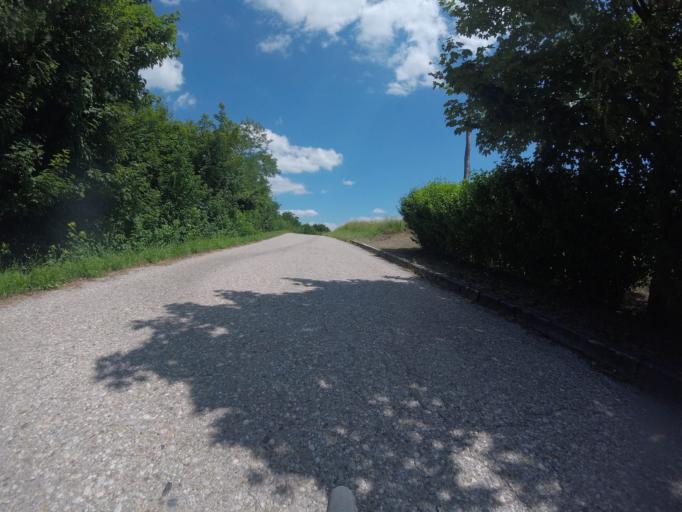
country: HR
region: Karlovacka
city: Ozalj
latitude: 45.6741
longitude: 15.4603
